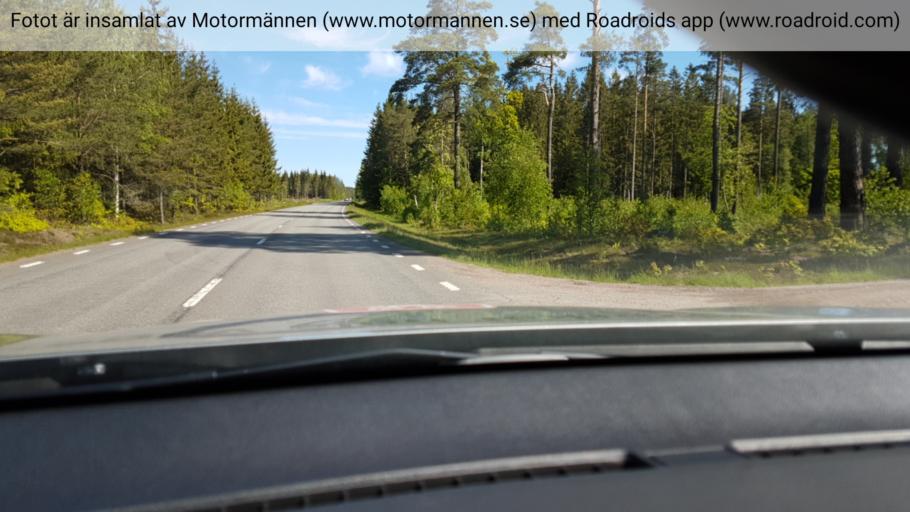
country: SE
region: Vaestra Goetaland
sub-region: Hjo Kommun
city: Hjo
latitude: 58.3901
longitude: 14.3526
